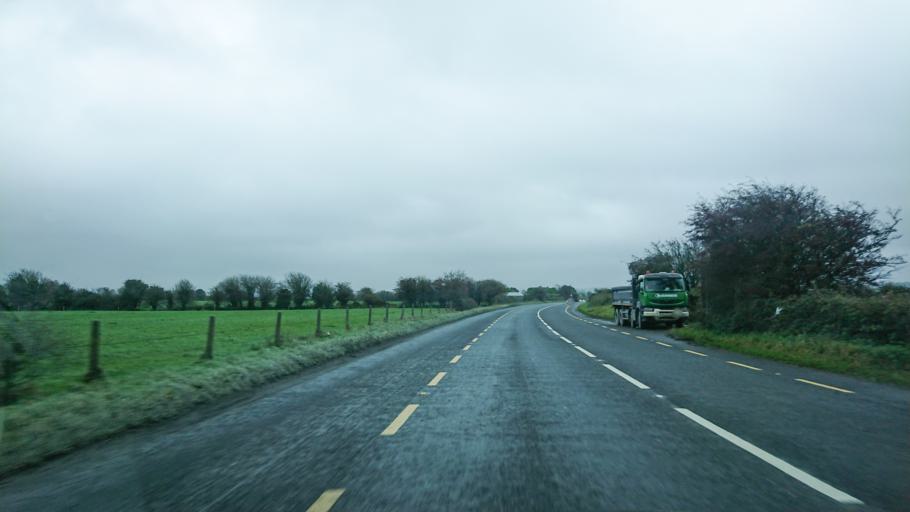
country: IE
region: Leinster
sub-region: Kilkenny
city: Mooncoin
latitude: 52.2825
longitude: -7.1845
